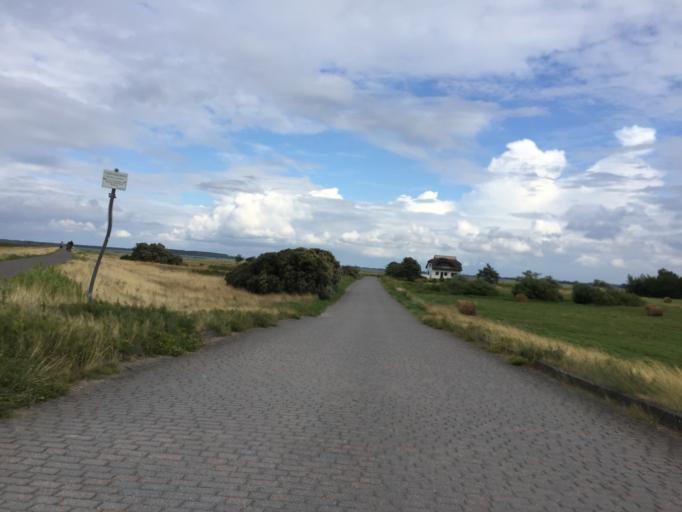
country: DE
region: Mecklenburg-Vorpommern
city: Hiddensee
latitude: 54.5607
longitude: 13.1054
